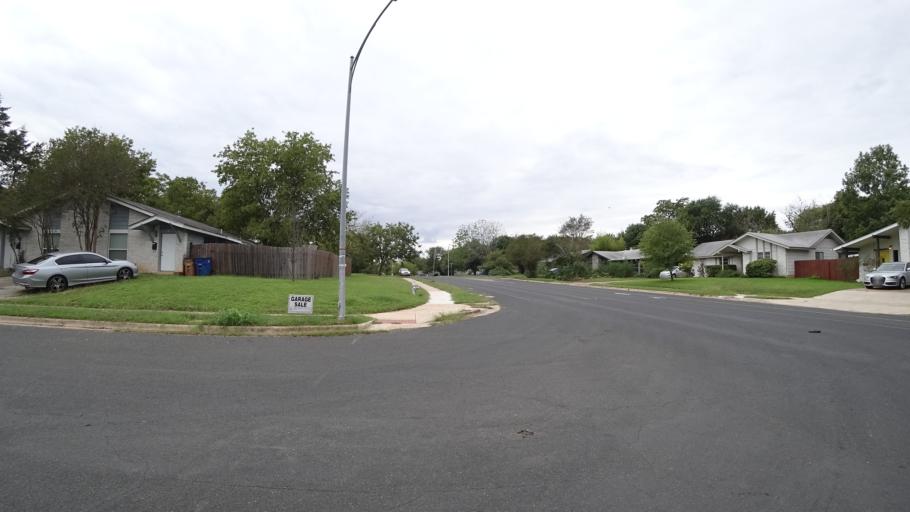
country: US
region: Texas
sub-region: Travis County
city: Rollingwood
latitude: 30.2163
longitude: -97.7841
